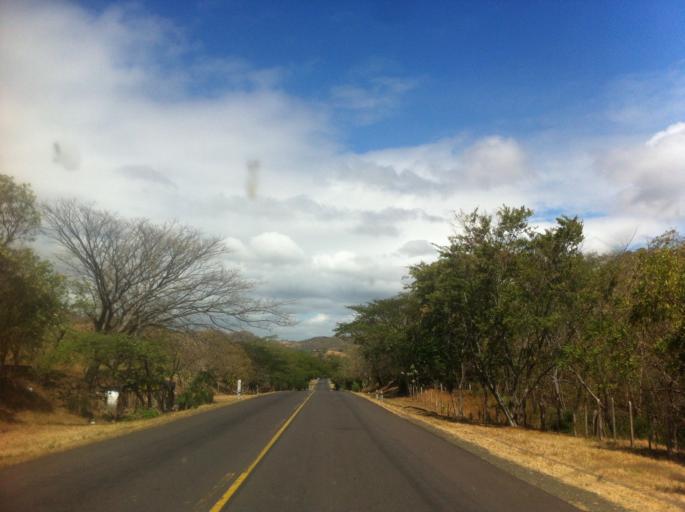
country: NI
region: Chontales
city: Acoyapa
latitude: 12.0223
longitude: -85.2555
